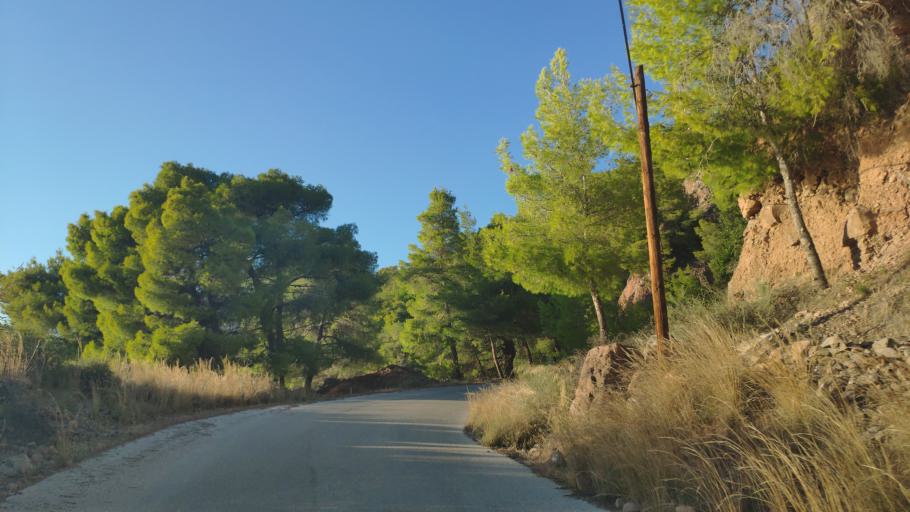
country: GR
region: Attica
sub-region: Nomos Piraios
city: Megalochori
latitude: 37.6063
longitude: 23.3309
